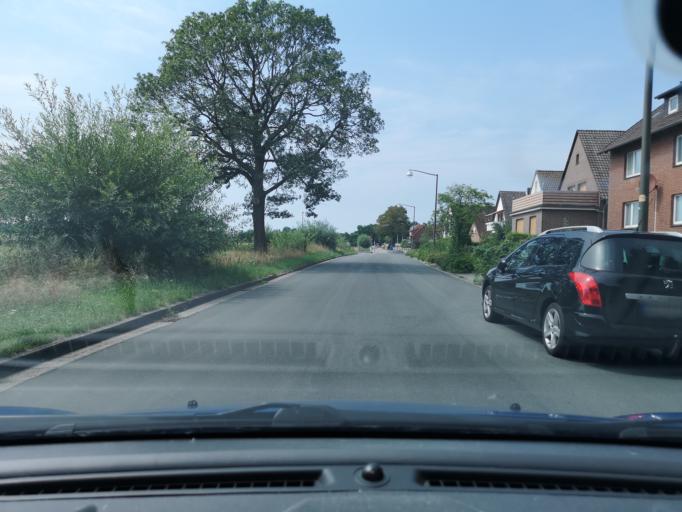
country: DE
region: Lower Saxony
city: Langenhagen
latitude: 52.4360
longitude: 9.7006
